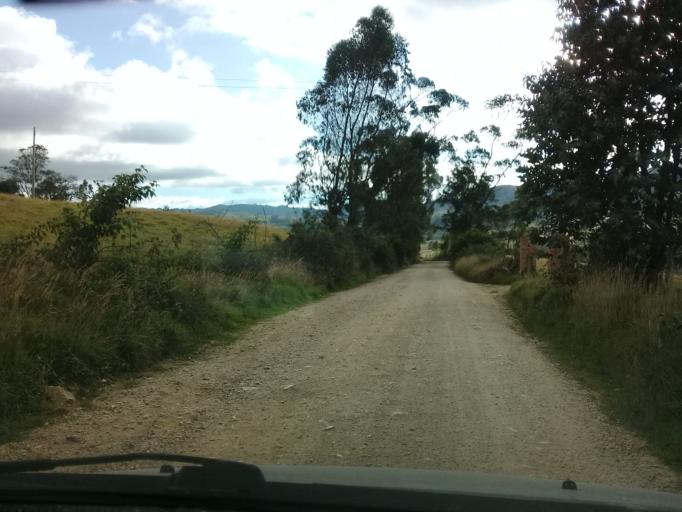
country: CO
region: Cundinamarca
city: Villapinzon
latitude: 5.2330
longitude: -73.6514
